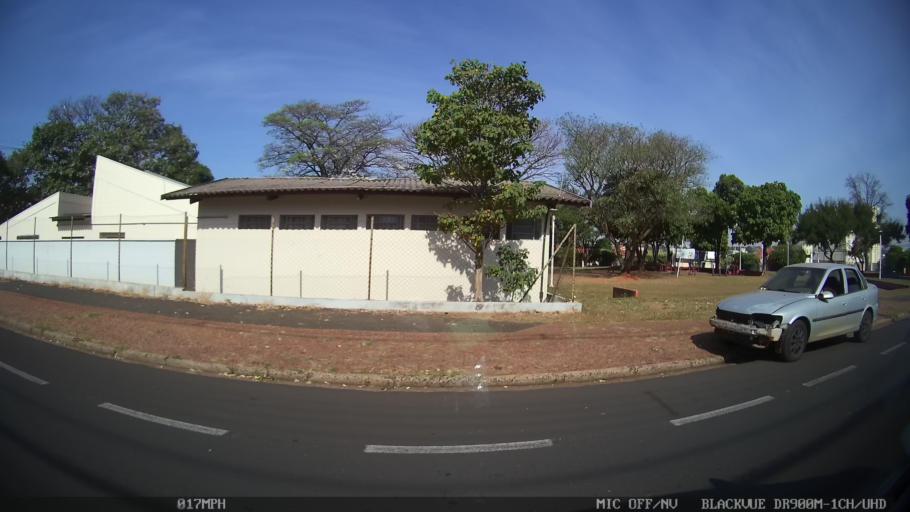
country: BR
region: Sao Paulo
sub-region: Sao Jose Do Rio Preto
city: Sao Jose do Rio Preto
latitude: -20.7965
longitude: -49.4102
